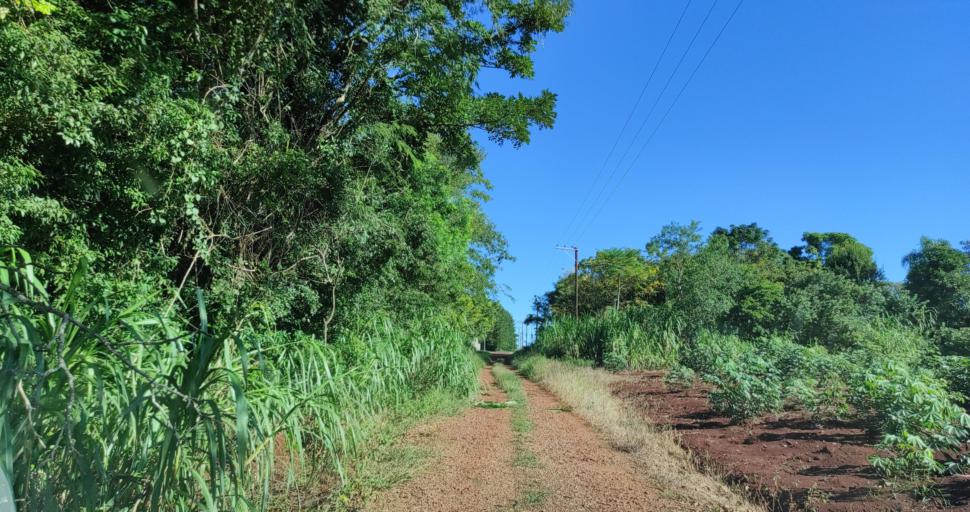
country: AR
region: Misiones
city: Capiovi
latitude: -26.9327
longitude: -55.0474
